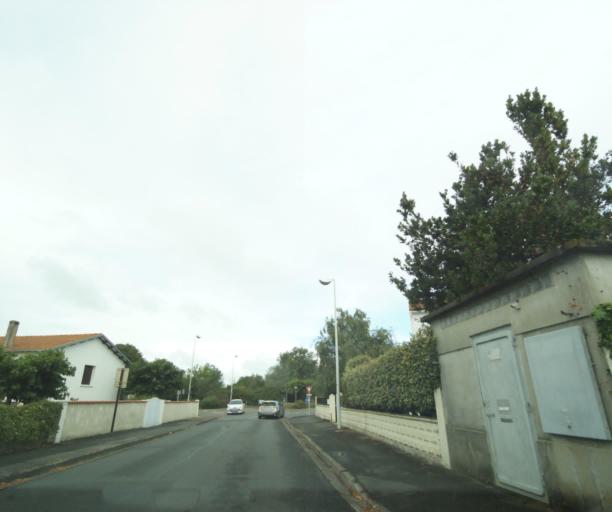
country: FR
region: Poitou-Charentes
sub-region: Departement de la Charente-Maritime
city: Lagord
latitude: 46.1875
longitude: -1.1582
